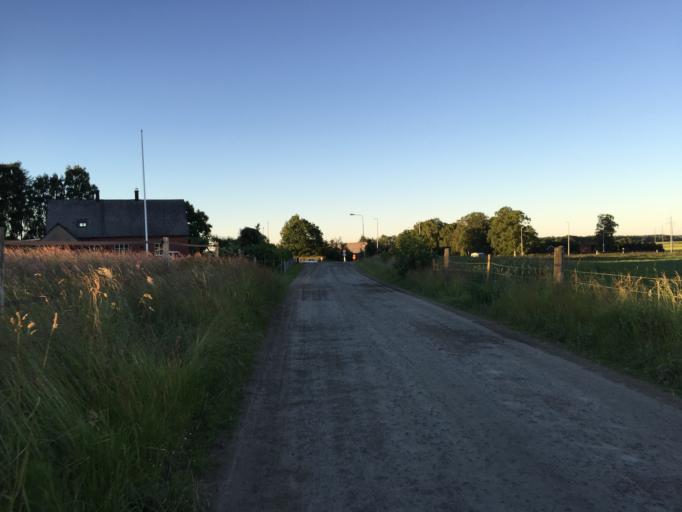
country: SE
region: Skane
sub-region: Lunds Kommun
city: Veberod
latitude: 55.6434
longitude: 13.4707
